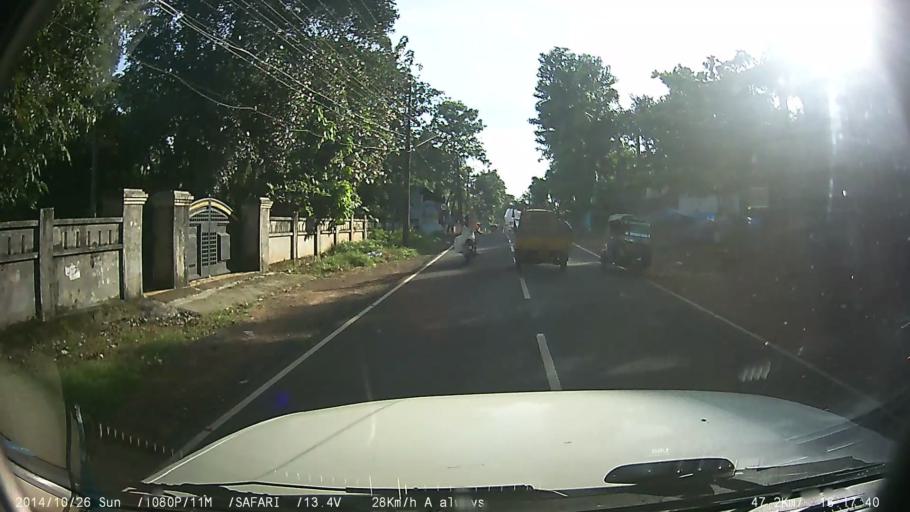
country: IN
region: Kerala
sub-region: Kottayam
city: Changanacheri
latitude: 9.4277
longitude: 76.5632
